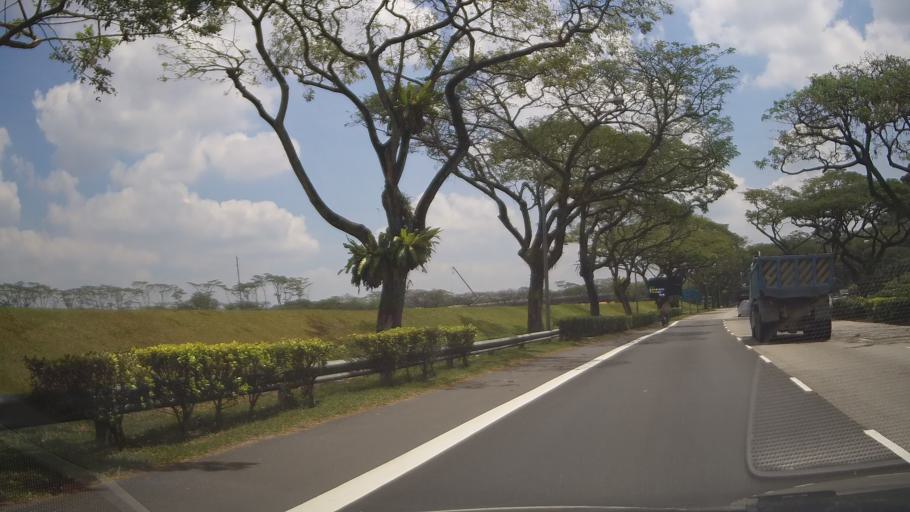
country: MY
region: Johor
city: Johor Bahru
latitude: 1.3535
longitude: 103.7143
